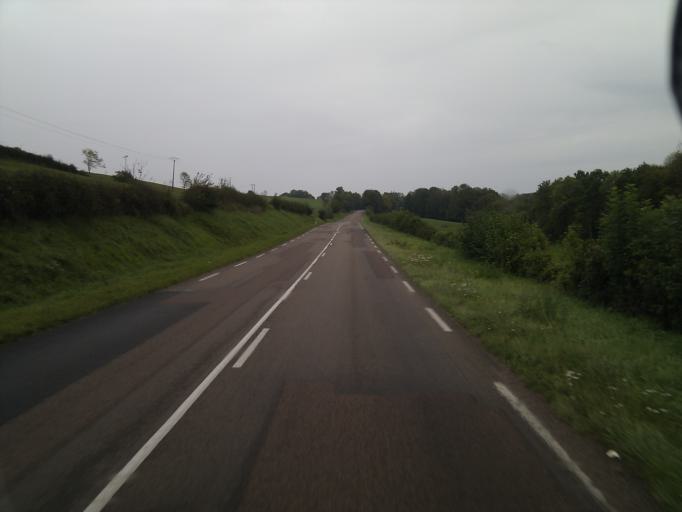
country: FR
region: Bourgogne
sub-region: Departement de la Cote-d'Or
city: Semur-en-Auxois
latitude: 47.5400
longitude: 4.3391
